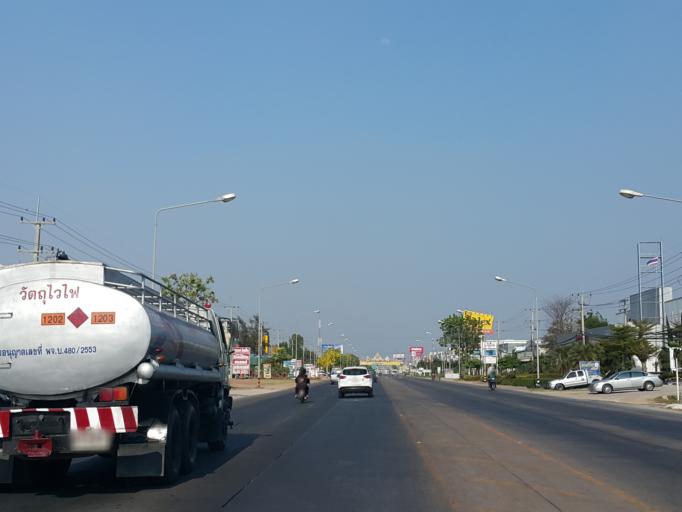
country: TH
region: Phitsanulok
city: Phitsanulok
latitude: 16.8166
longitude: 100.3109
